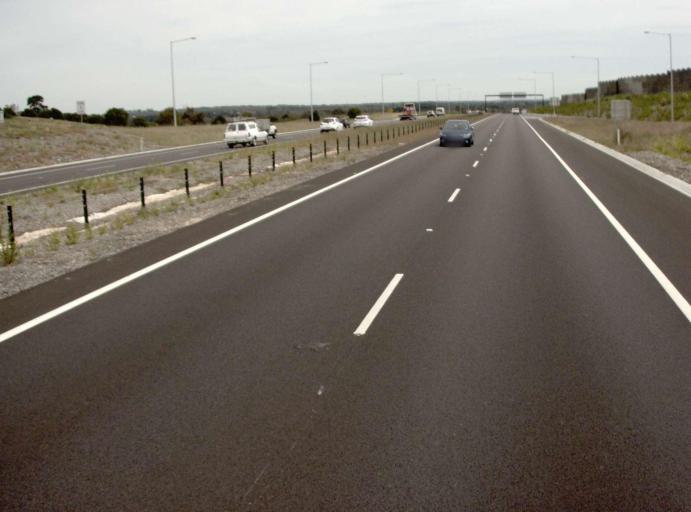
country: AU
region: Victoria
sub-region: Frankston
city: Langwarrin
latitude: -38.1826
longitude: 145.1586
